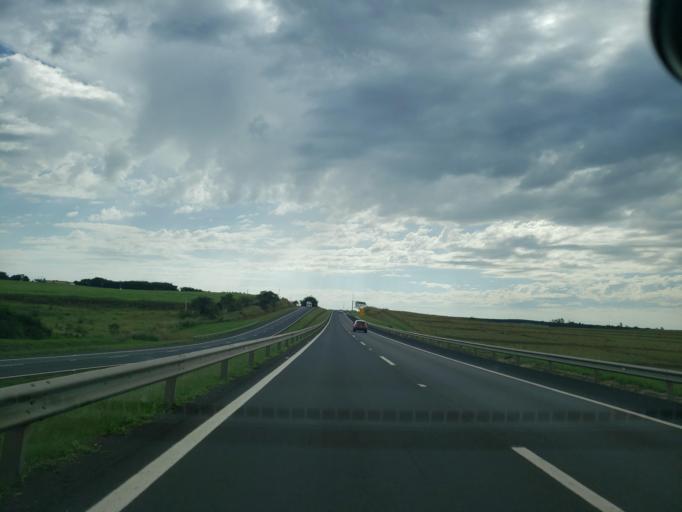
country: BR
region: Sao Paulo
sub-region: Cafelandia
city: Cafelandia
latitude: -21.7785
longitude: -49.6602
